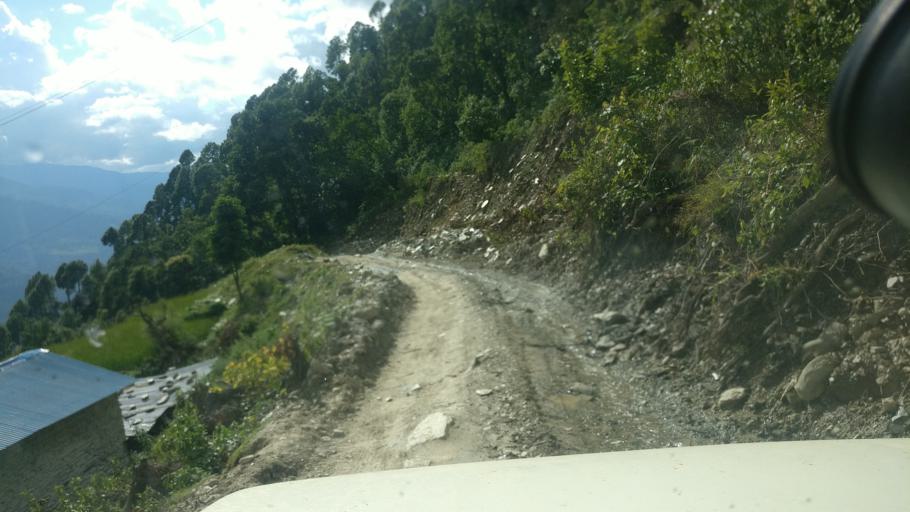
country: NP
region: Western Region
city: Baglung
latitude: 28.2752
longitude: 83.6425
